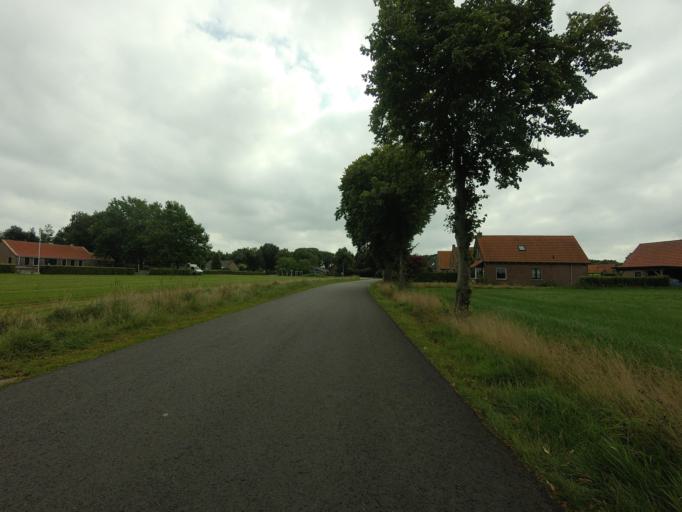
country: NL
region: Overijssel
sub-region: Gemeente Steenwijkerland
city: Steenwijkerwold
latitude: 52.8055
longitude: 6.0319
